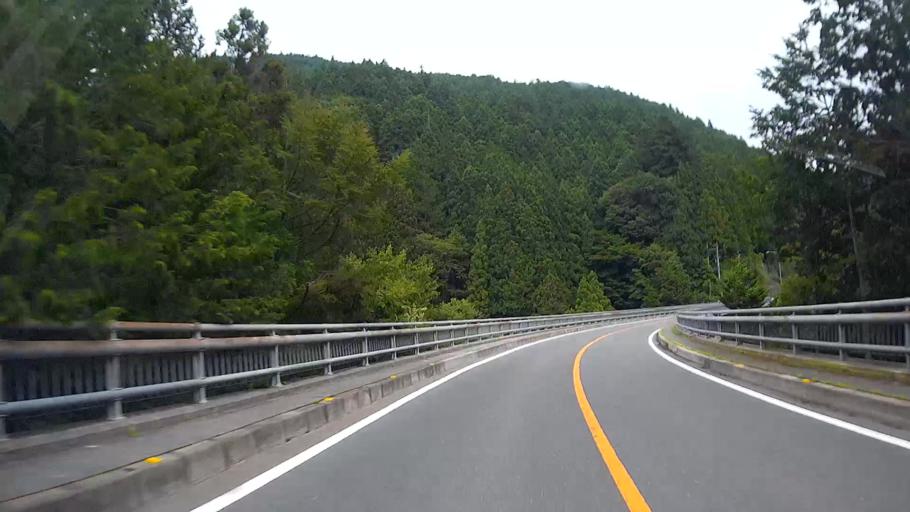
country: JP
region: Saitama
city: Chichibu
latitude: 35.9379
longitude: 138.8473
